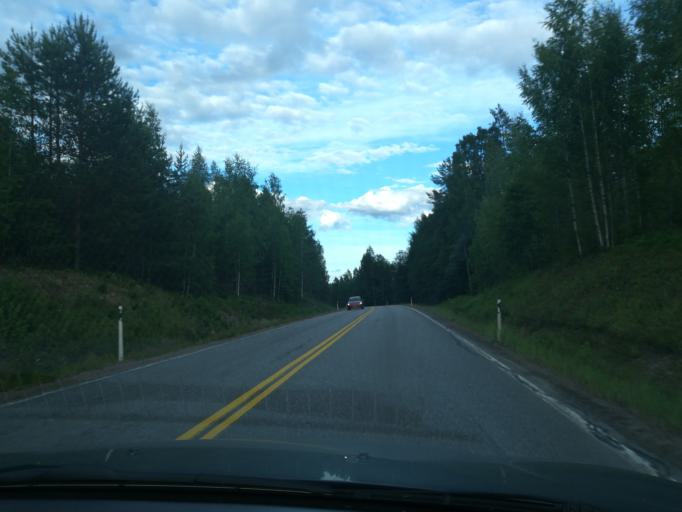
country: FI
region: Southern Savonia
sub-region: Mikkeli
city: Puumala
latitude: 61.5631
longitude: 28.1035
